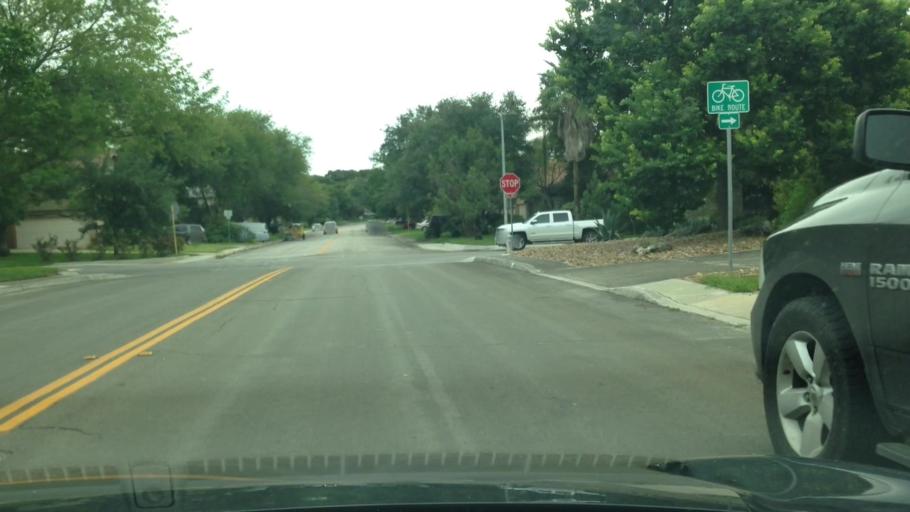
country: US
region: Texas
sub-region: Bexar County
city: Hollywood Park
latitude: 29.5730
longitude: -98.4283
